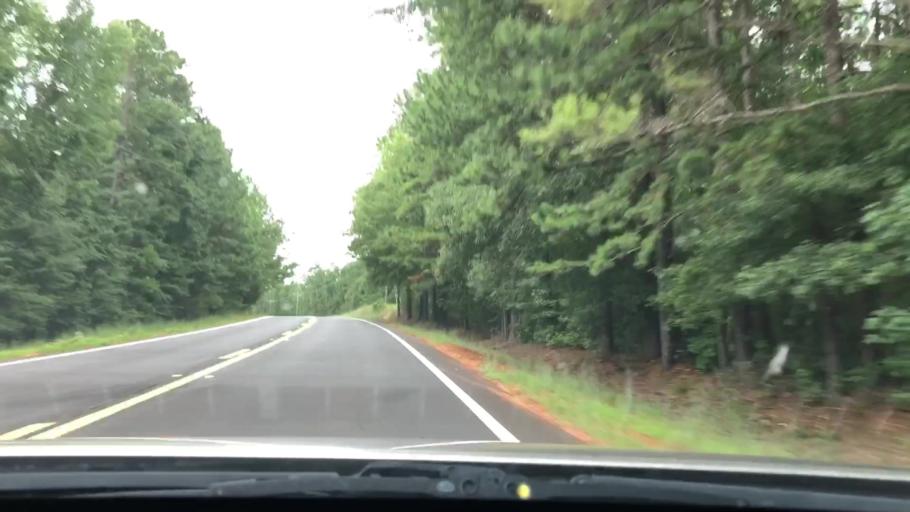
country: US
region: Georgia
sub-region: Upson County
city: Hannahs Mill
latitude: 33.0148
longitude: -84.4202
